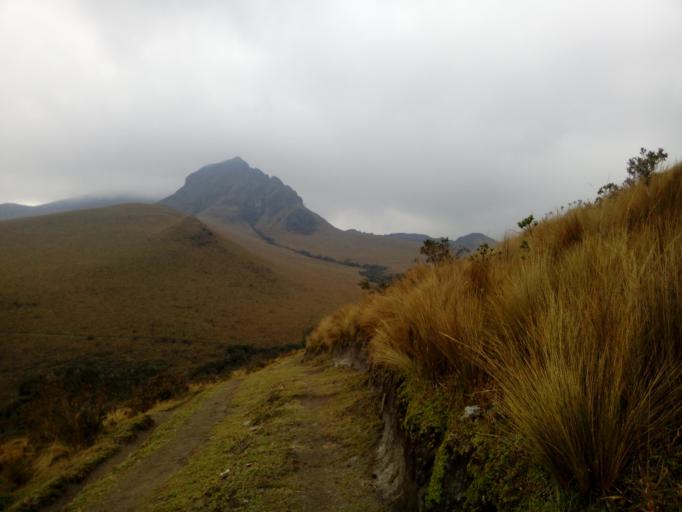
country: EC
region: Pichincha
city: Machachi
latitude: -0.5576
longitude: -78.5281
